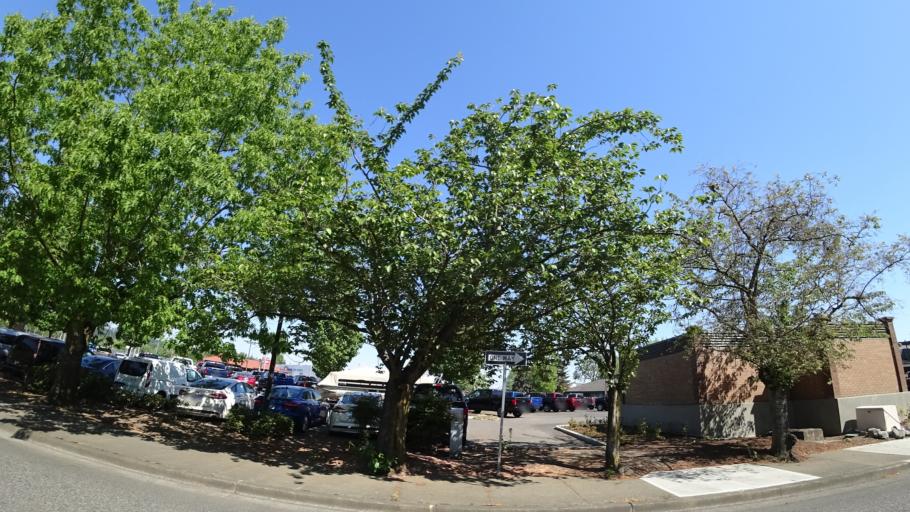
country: US
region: Oregon
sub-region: Washington County
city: Beaverton
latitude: 45.4902
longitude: -122.8059
